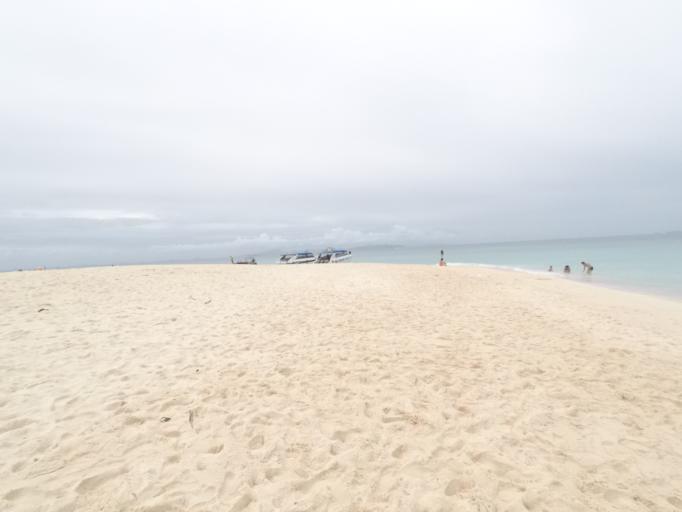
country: TH
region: Phangnga
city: Ban Ao Nang
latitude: 7.8191
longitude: 98.7985
